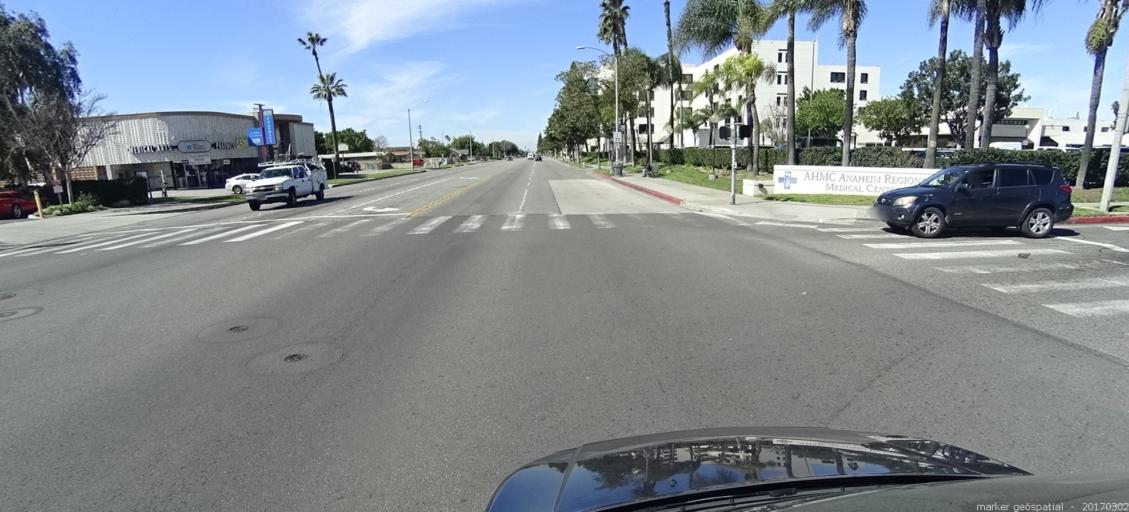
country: US
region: California
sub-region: Orange County
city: Anaheim
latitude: 33.8472
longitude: -117.9320
